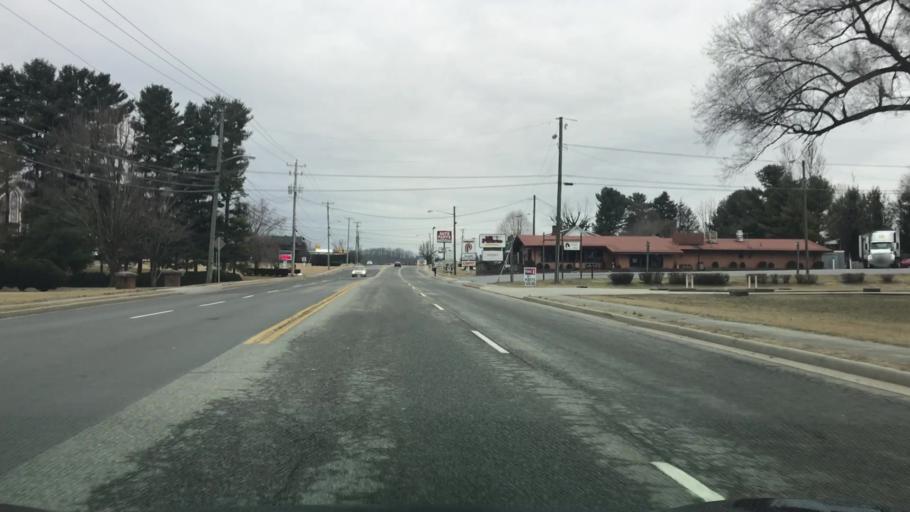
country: US
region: Virginia
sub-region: Smyth County
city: Marion
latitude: 36.8455
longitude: -81.4960
